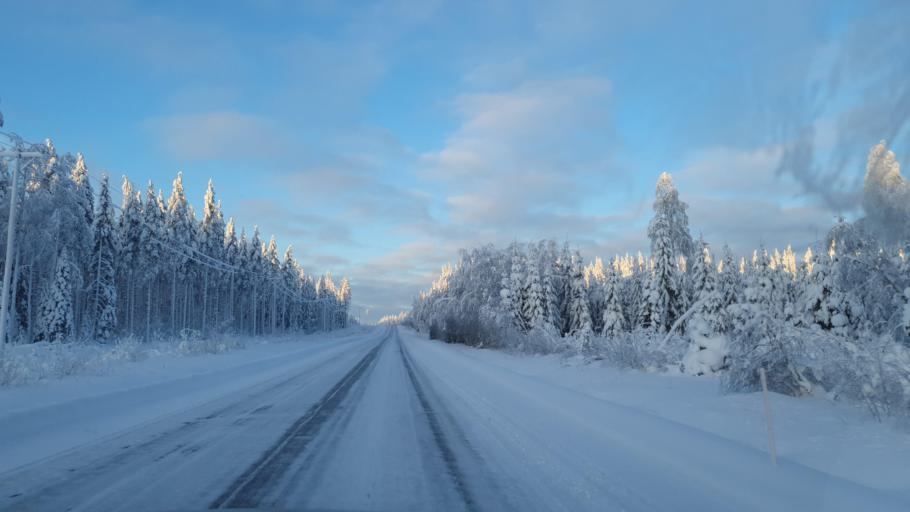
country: FI
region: Kainuu
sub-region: Kajaani
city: Vuokatti
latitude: 64.2280
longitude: 28.2440
